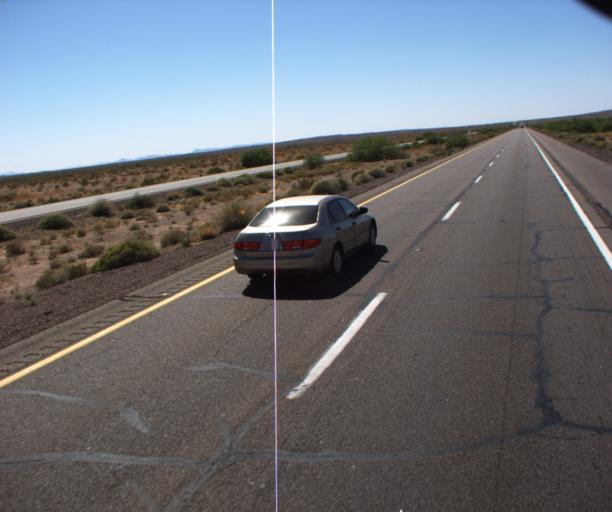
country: US
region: Arizona
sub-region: Maricopa County
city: Gila Bend
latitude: 32.8880
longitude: -113.0767
